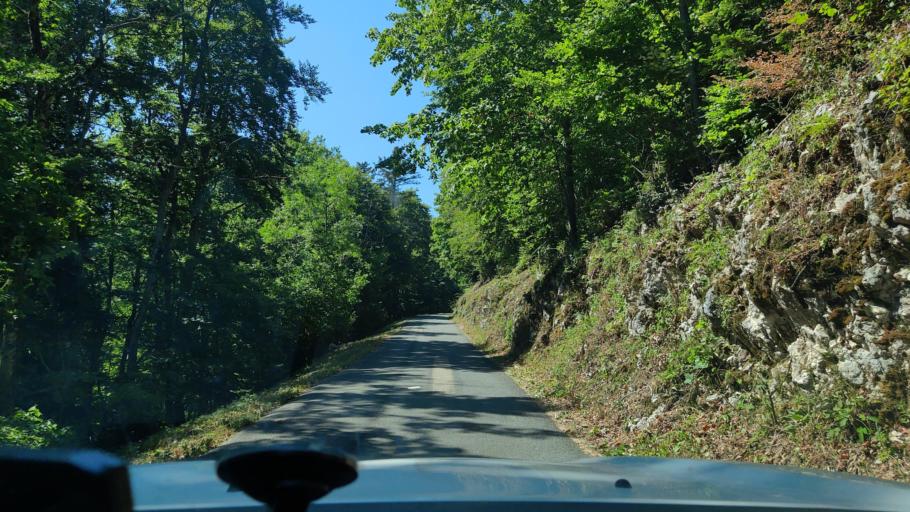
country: FR
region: Rhone-Alpes
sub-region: Departement de la Savoie
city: Le Bourget-du-Lac
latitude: 45.6499
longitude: 5.8275
